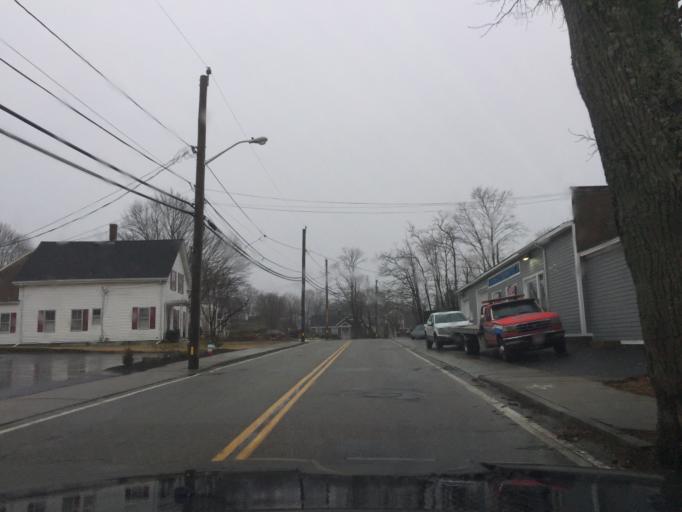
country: US
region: Massachusetts
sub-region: Plymouth County
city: Plymouth
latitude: 41.9500
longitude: -70.6599
